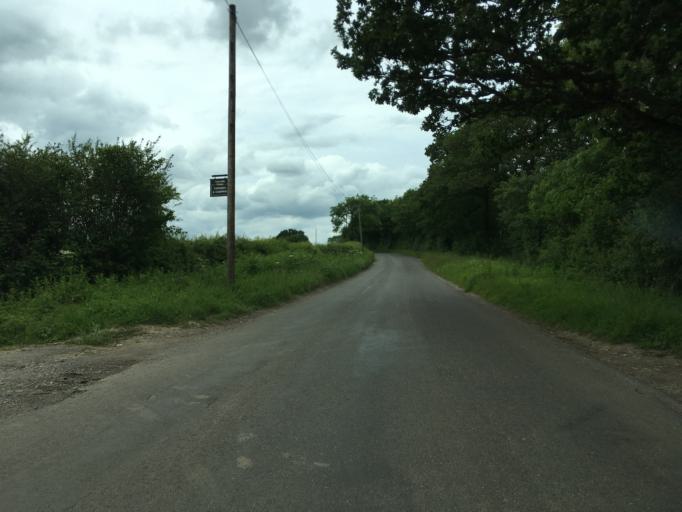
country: GB
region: England
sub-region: Wiltshire
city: Malmesbury
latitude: 51.5207
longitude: -2.1010
